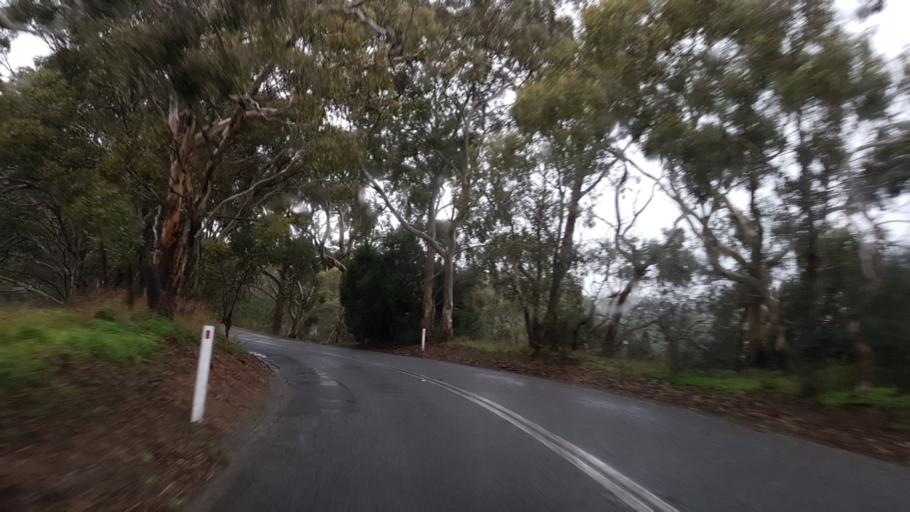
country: AU
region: South Australia
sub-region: Onkaparinga
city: Craigburn Farm
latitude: -35.0869
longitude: 138.6157
